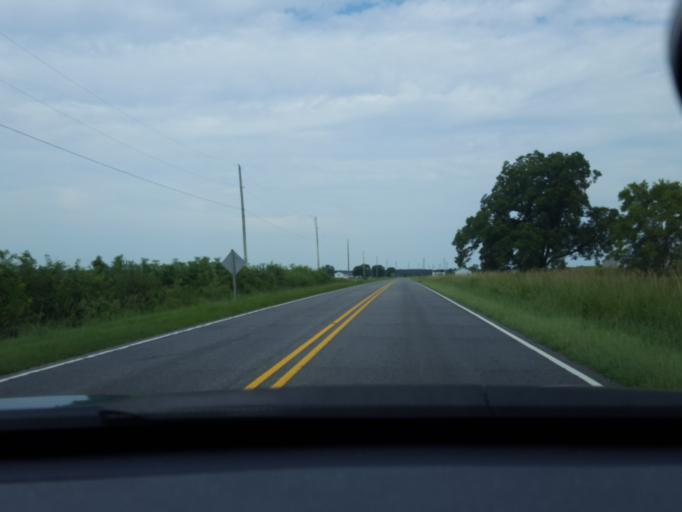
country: US
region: North Carolina
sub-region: Chowan County
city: Edenton
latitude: 36.1065
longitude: -76.6366
